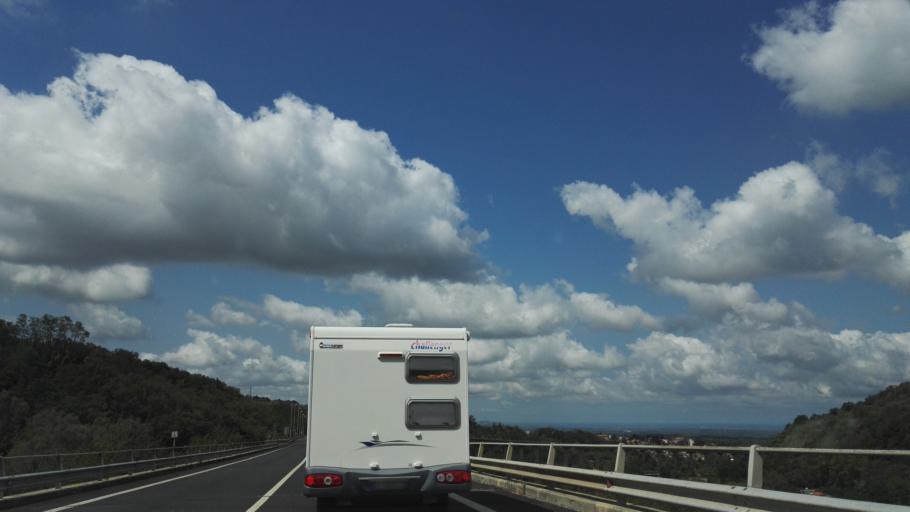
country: IT
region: Calabria
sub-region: Provincia di Reggio Calabria
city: Anoia Superiore
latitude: 38.4173
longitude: 16.1141
